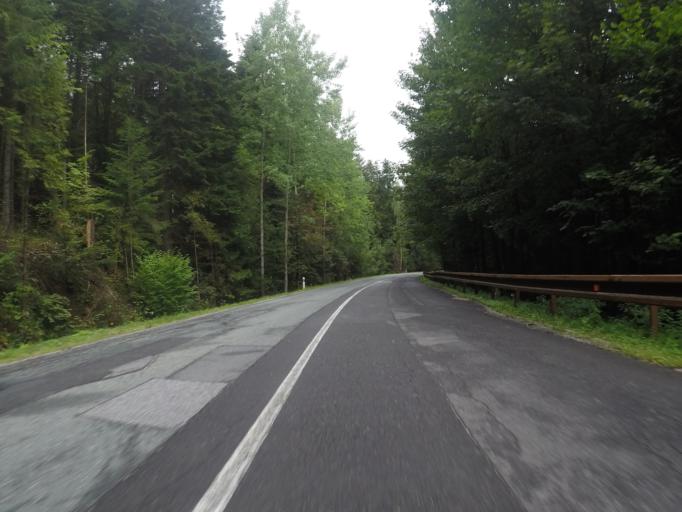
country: SK
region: Kosicky
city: Spisska Nova Ves
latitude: 48.8923
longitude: 20.5305
